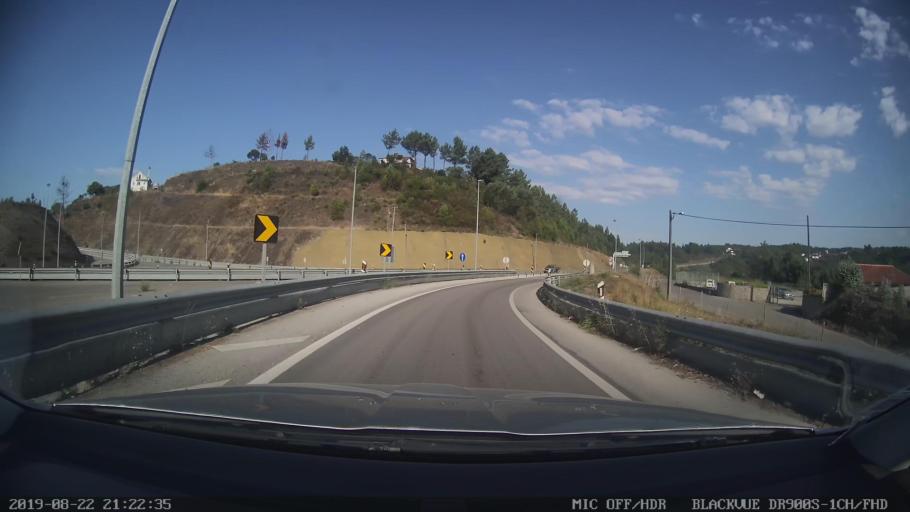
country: PT
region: Castelo Branco
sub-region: Serta
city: Serta
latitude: 39.8217
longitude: -8.1017
